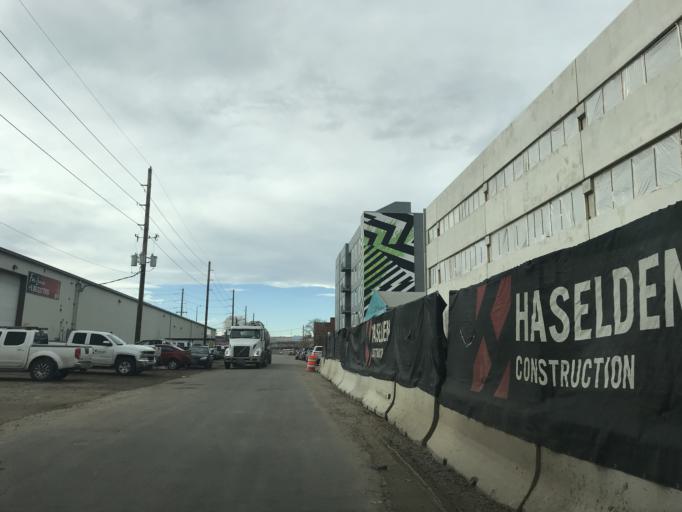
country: US
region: Colorado
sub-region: Denver County
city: Denver
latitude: 39.7715
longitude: -104.9757
